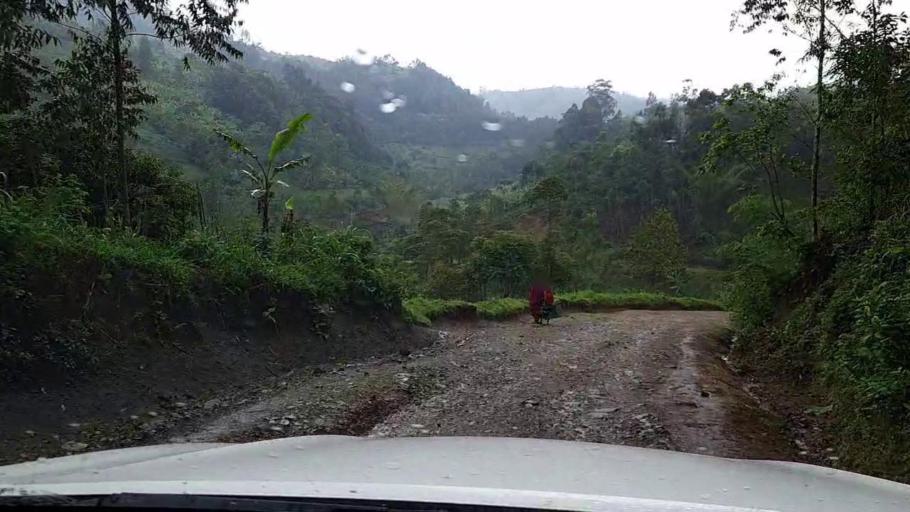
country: RW
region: Western Province
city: Cyangugu
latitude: -2.5334
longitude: 29.0420
